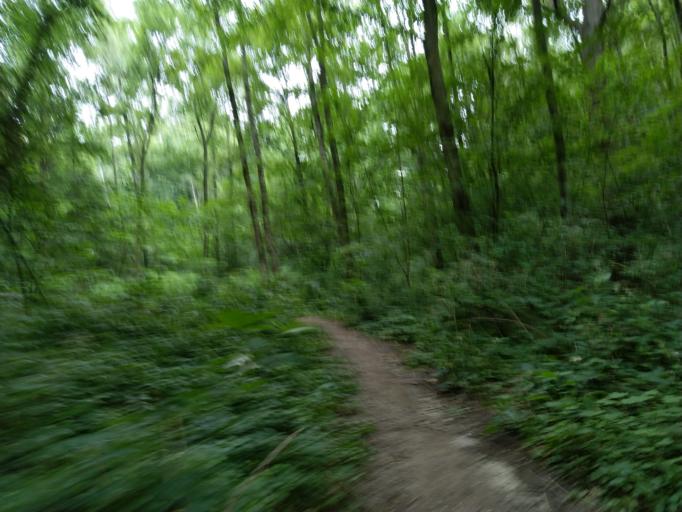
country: BE
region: Wallonia
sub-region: Province du Hainaut
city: Mons
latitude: 50.4957
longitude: 3.9493
